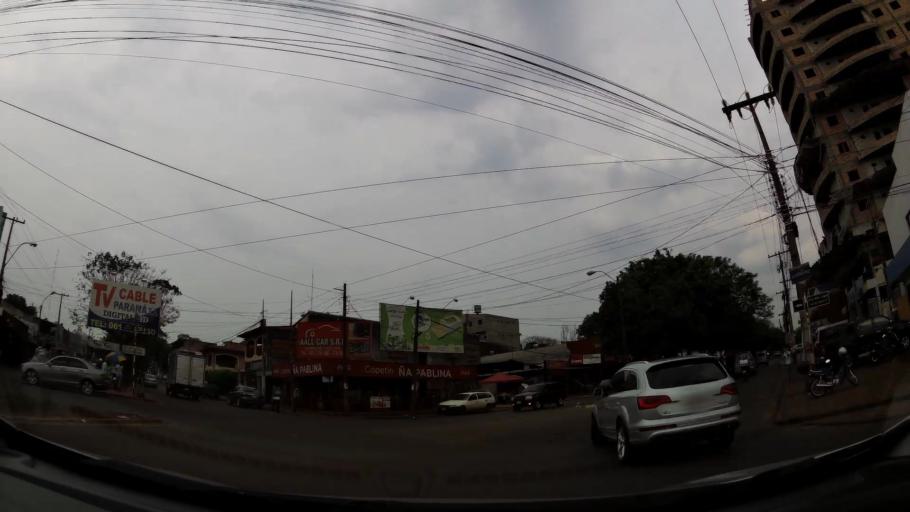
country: PY
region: Alto Parana
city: Presidente Franco
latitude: -25.5160
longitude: -54.6424
